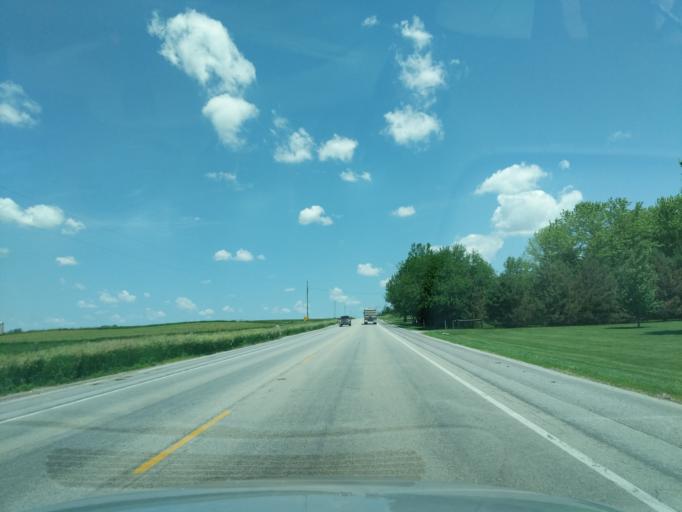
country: US
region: Indiana
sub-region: LaGrange County
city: Topeka
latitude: 41.6197
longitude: -85.5796
